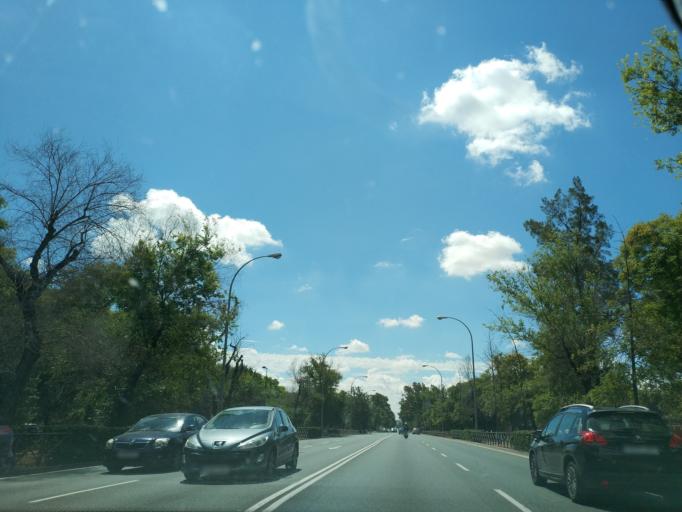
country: ES
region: Andalusia
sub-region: Provincia de Sevilla
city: Sevilla
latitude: 37.3665
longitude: -5.9657
